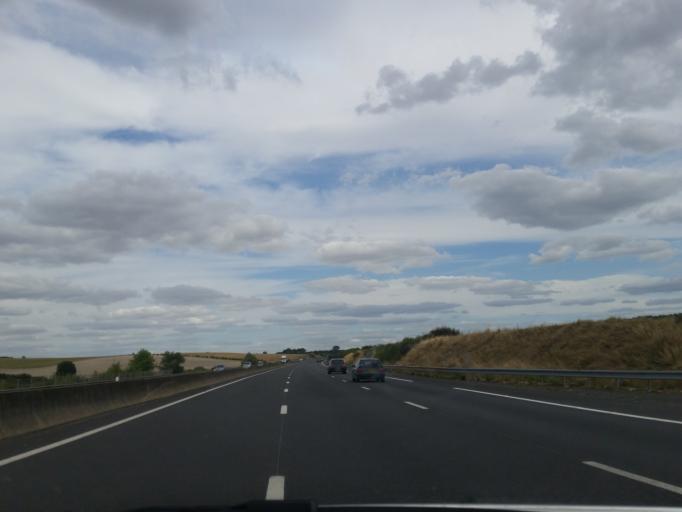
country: FR
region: Centre
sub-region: Departement d'Indre-et-Loire
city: Auzouer-en-Touraine
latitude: 47.5207
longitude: 0.9219
